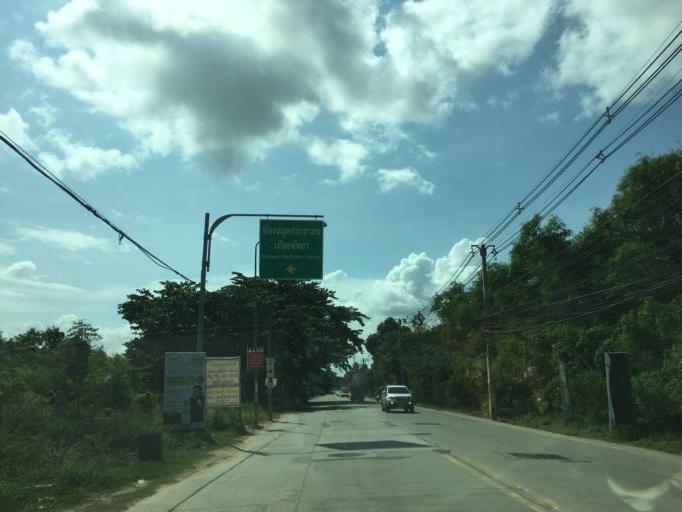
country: TH
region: Chon Buri
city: Phatthaya
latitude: 12.8903
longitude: 100.8909
